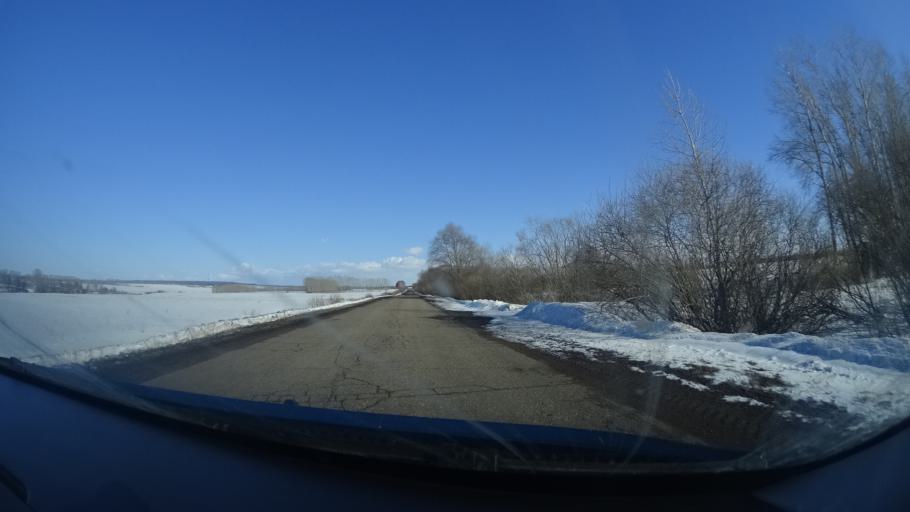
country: RU
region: Bashkortostan
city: Chishmy
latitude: 54.5886
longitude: 55.2650
